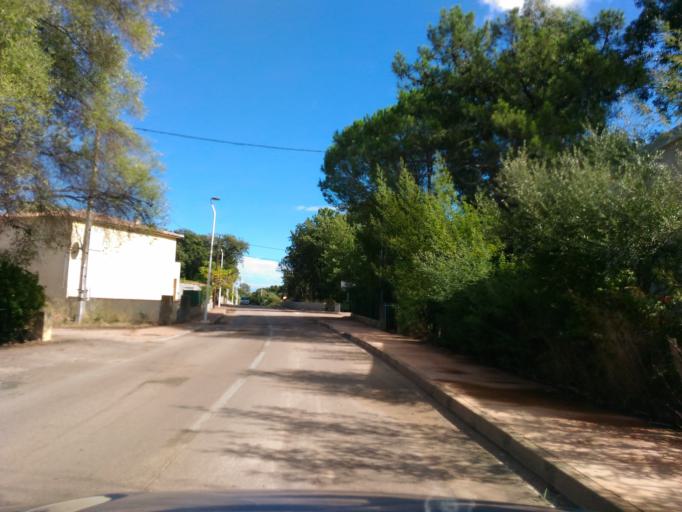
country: FR
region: Corsica
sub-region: Departement de la Corse-du-Sud
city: Porto-Vecchio
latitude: 41.7009
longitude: 9.3413
